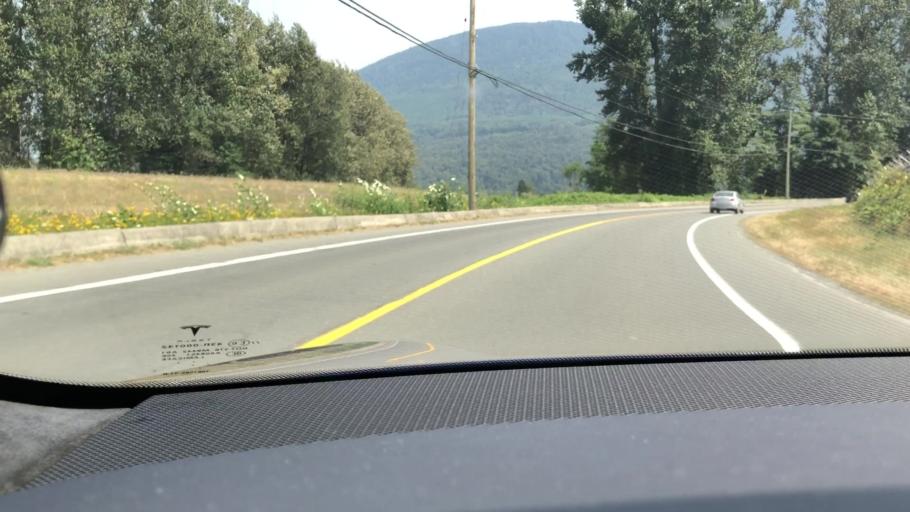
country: CA
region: British Columbia
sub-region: Fraser Valley Regional District
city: Chilliwack
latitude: 49.0890
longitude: -122.0657
